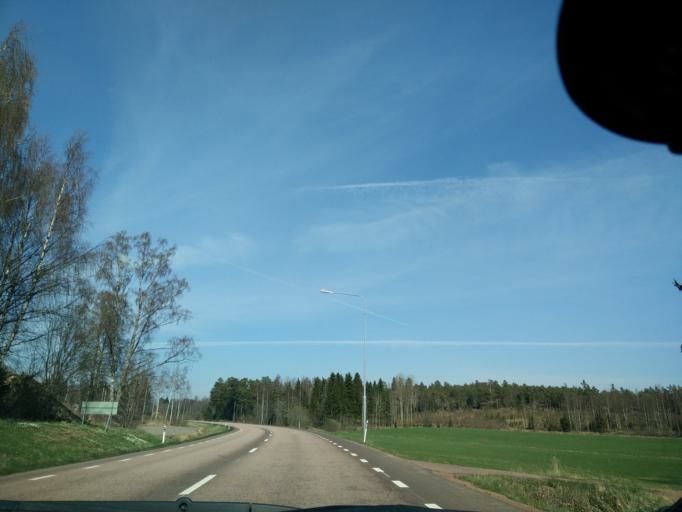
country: AX
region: Alands landsbygd
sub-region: Finstroem
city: Finstroem
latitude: 60.2170
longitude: 19.9809
